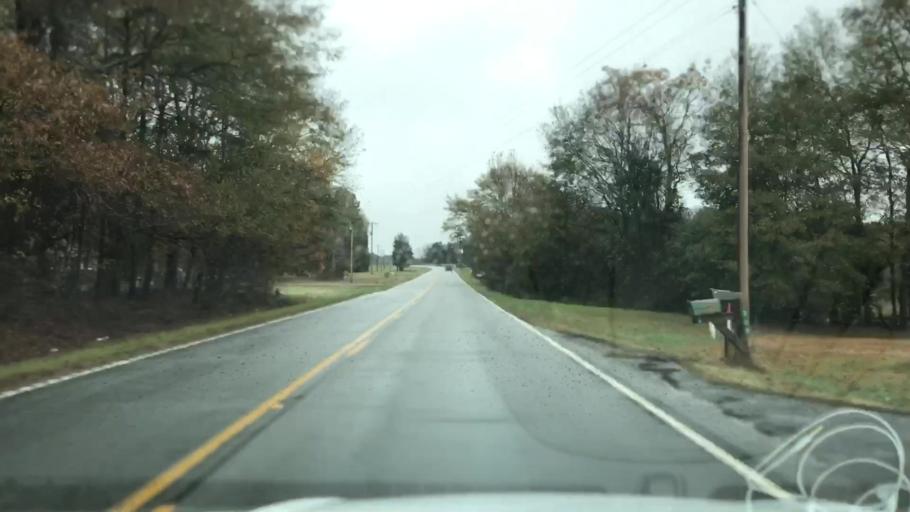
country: US
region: South Carolina
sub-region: Spartanburg County
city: Roebuck
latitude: 34.8244
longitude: -81.9238
